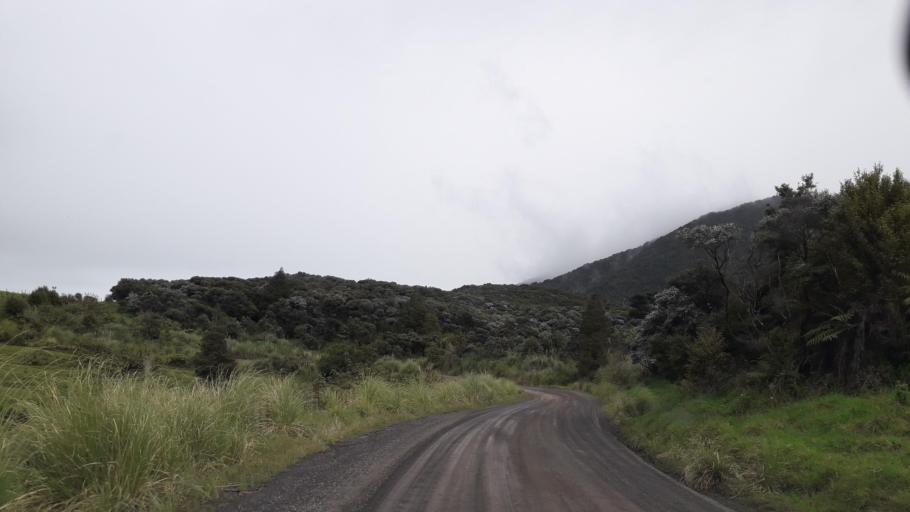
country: NZ
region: Northland
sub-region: Far North District
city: Kaitaia
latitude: -35.4070
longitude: 173.3642
